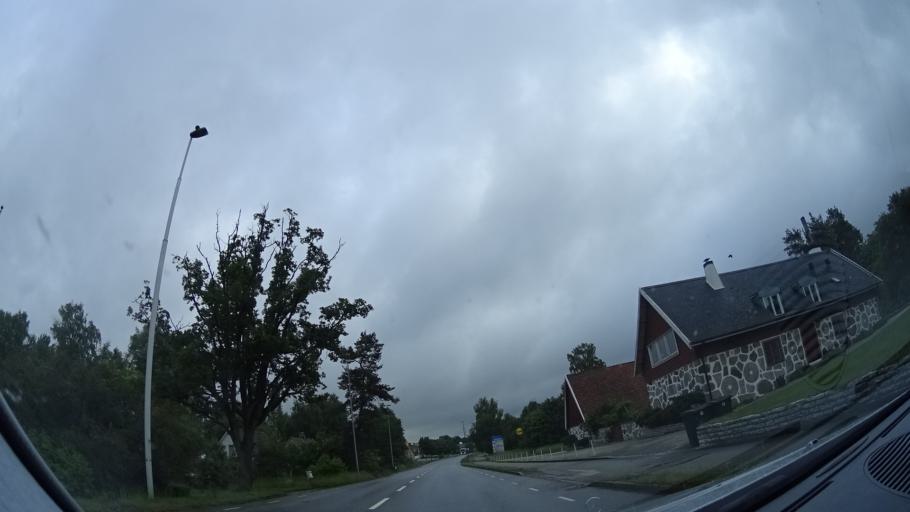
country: SE
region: Skane
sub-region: Hoors Kommun
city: Satofta
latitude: 55.9244
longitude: 13.5432
